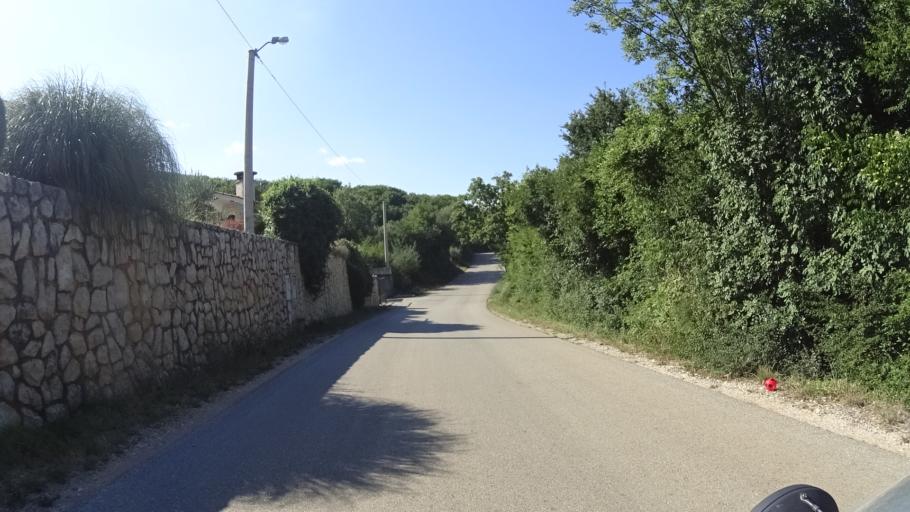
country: HR
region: Istarska
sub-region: Grad Labin
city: Rabac
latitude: 45.0124
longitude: 14.1552
